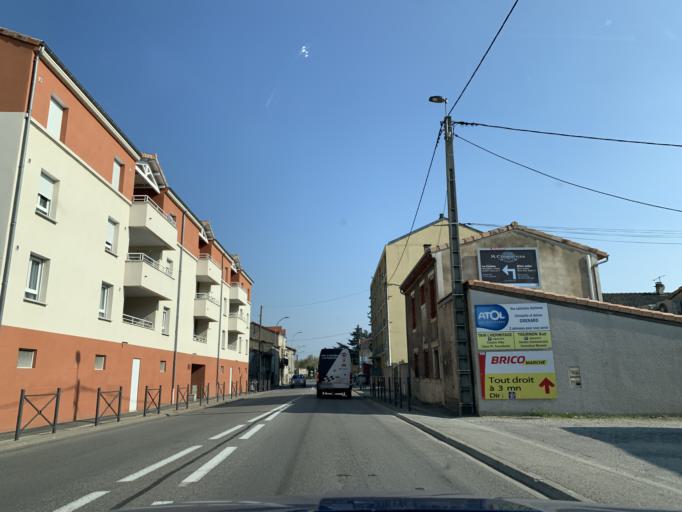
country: FR
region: Rhone-Alpes
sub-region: Departement de l'Ardeche
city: Tournon-sur-Rhone
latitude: 45.0738
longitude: 4.8319
